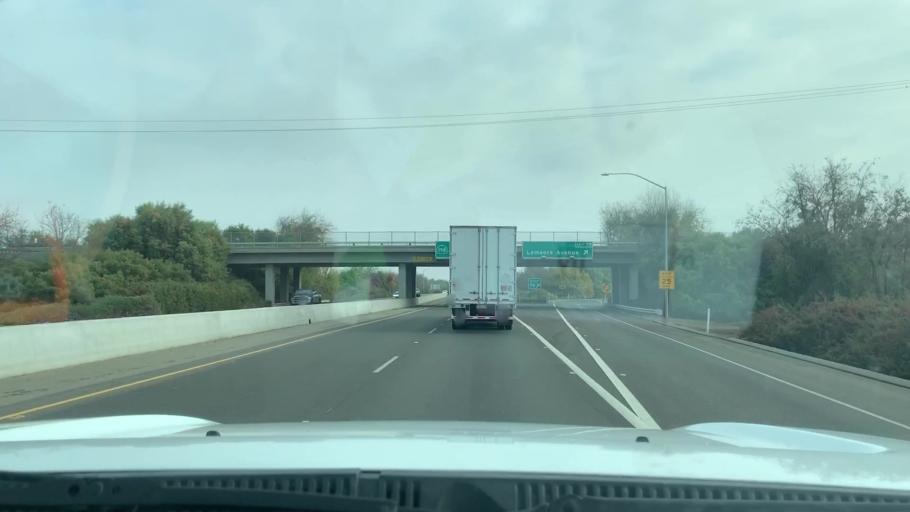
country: US
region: California
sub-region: Kings County
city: Lemoore
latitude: 36.2916
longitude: -119.7817
